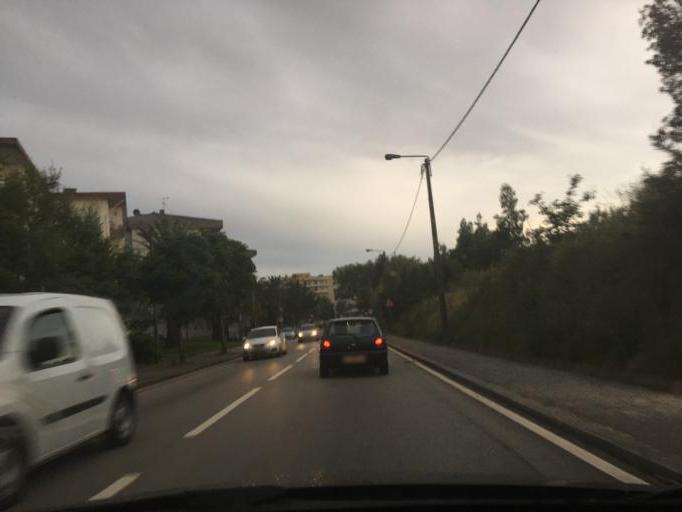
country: PT
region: Porto
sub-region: Maia
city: Anta
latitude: 41.2686
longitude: -8.6113
